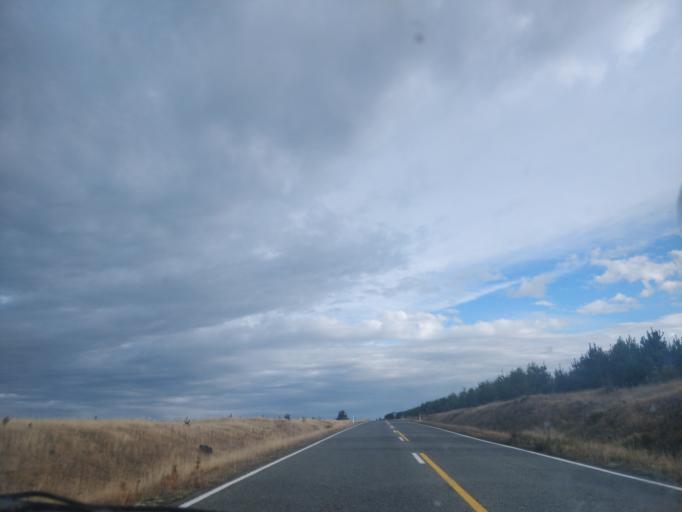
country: NZ
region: Canterbury
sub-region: Timaru District
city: Pleasant Point
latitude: -44.0908
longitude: 170.1349
